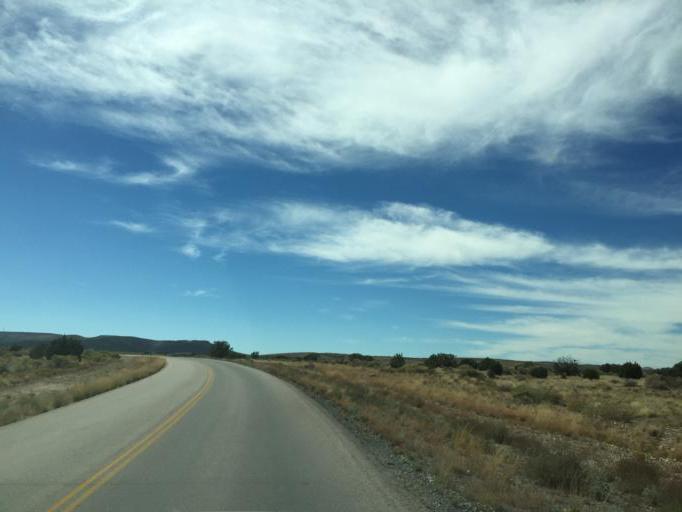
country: US
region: Arizona
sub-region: Mohave County
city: Meadview
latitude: 35.9563
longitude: -113.8440
